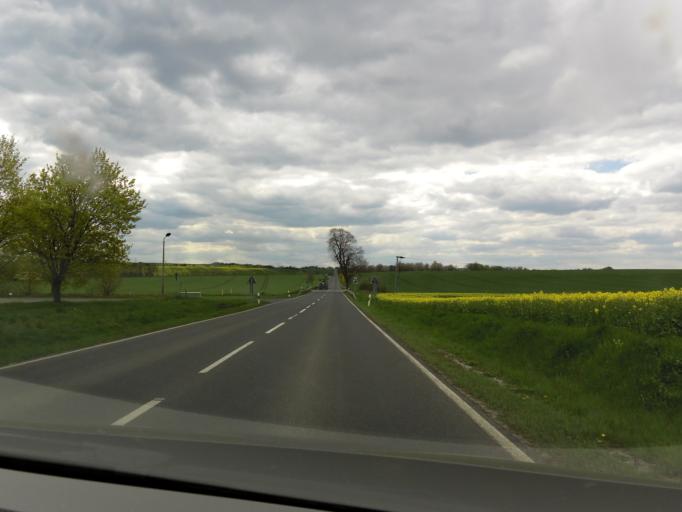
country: DE
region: Saxony-Anhalt
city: Eckartsberga
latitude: 51.1065
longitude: 11.5511
